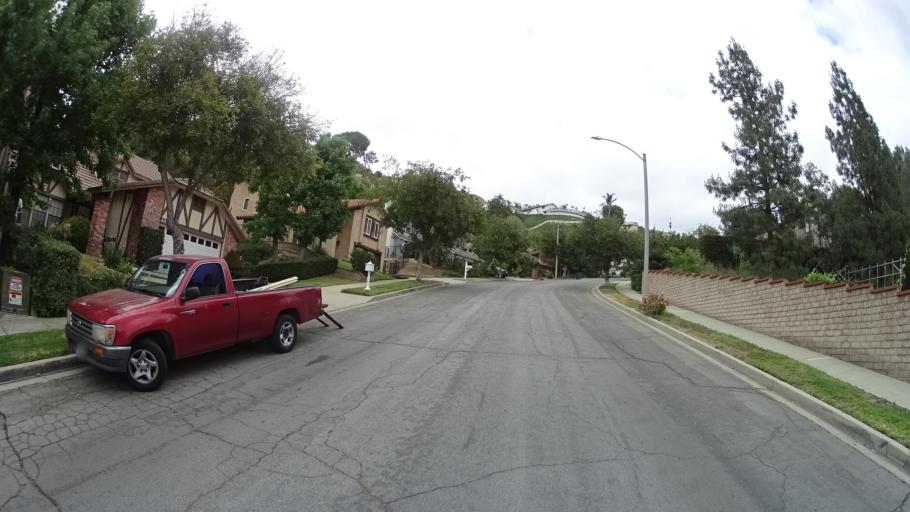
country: US
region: California
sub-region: Los Angeles County
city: Burbank
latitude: 34.2060
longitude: -118.3253
